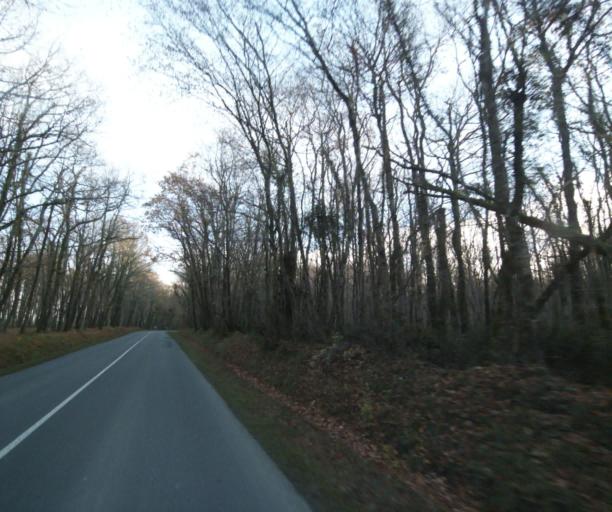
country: FR
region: Poitou-Charentes
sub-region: Departement de la Charente-Maritime
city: Fontcouverte
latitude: 45.7756
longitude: -0.5622
